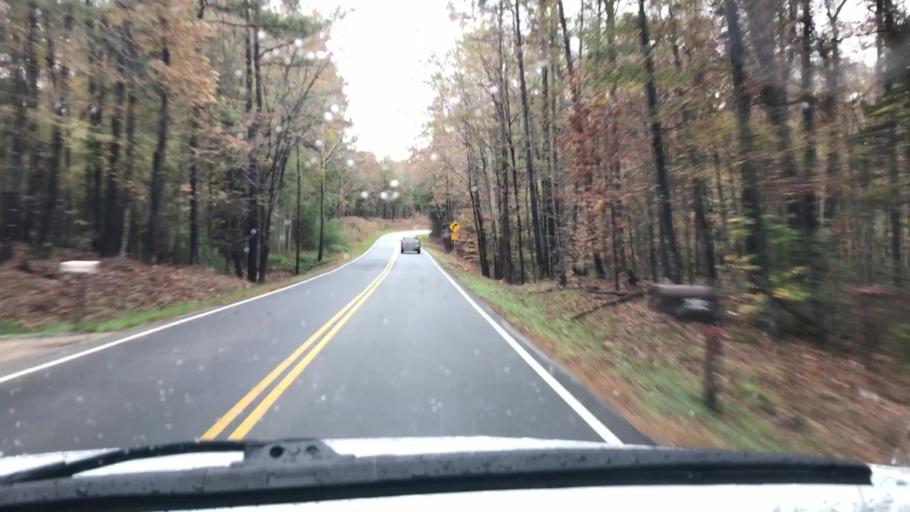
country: US
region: Virginia
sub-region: Henrico County
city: Short Pump
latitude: 37.6074
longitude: -77.6989
